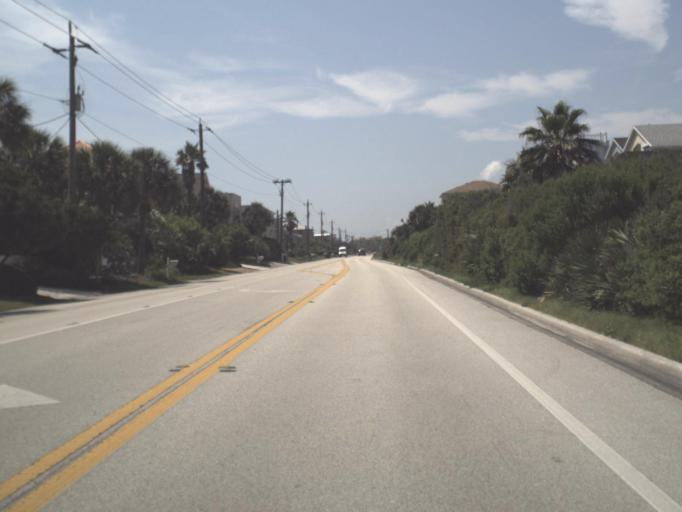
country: US
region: Florida
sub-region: Saint Johns County
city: Villano Beach
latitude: 29.9784
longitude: -81.3122
